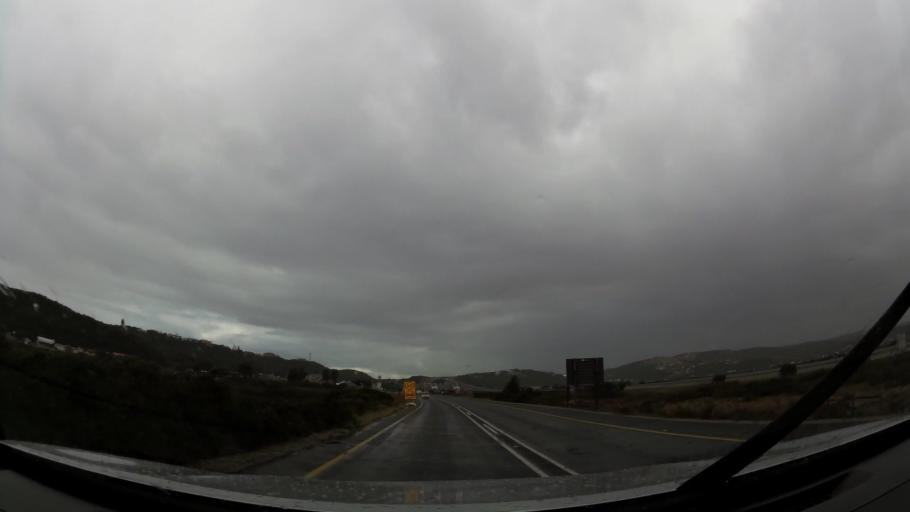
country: ZA
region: Western Cape
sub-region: Eden District Municipality
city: Mossel Bay
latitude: -34.0521
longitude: 22.2293
